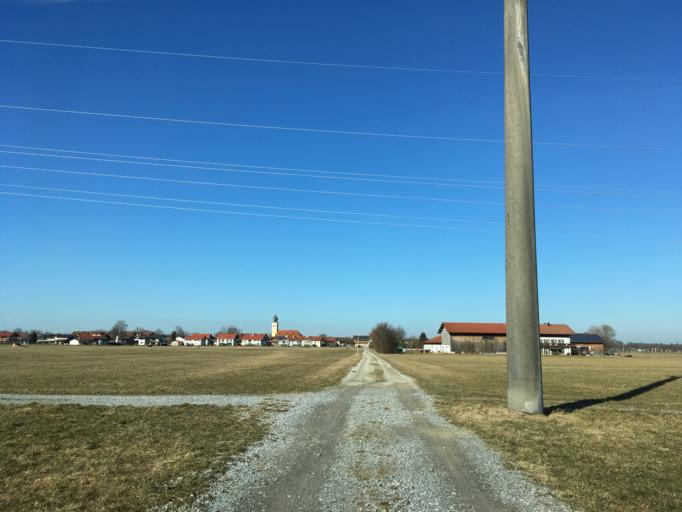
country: DE
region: Bavaria
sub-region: Upper Bavaria
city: Irschenberg
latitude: 47.8574
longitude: 11.9457
